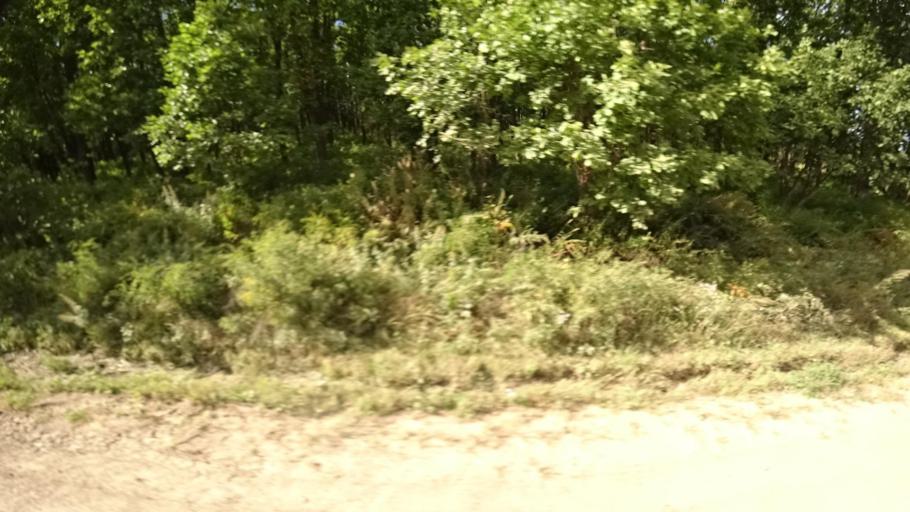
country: RU
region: Primorskiy
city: Yakovlevka
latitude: 44.3850
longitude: 133.5375
